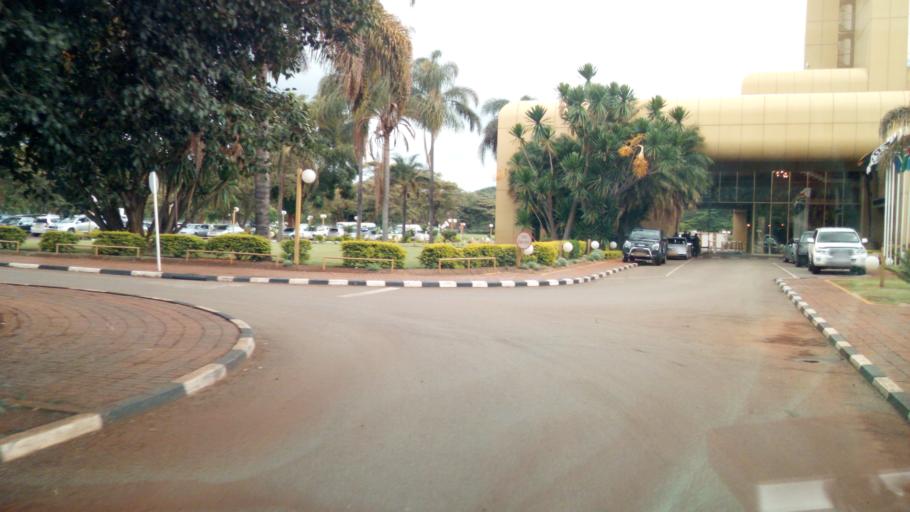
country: ZW
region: Harare
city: Harare
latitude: -17.8306
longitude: 31.0359
